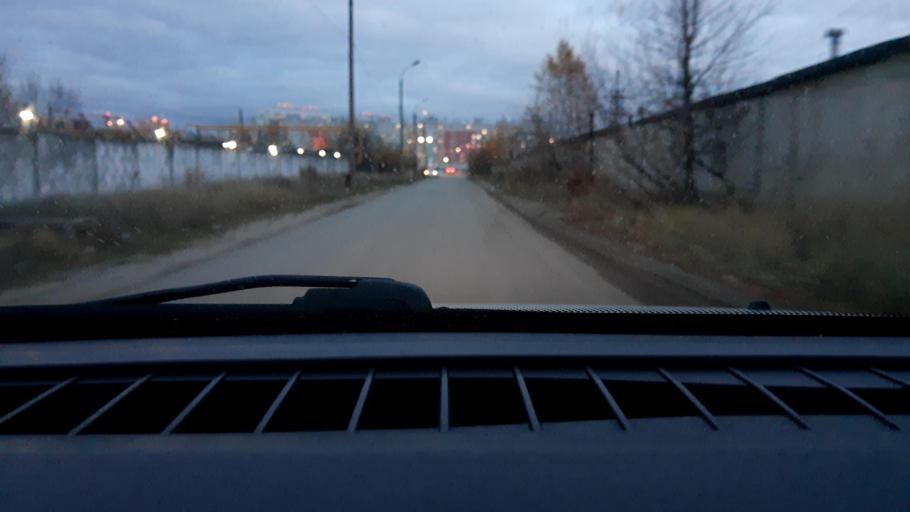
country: RU
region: Nizjnij Novgorod
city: Gorbatovka
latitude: 56.3628
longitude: 43.7904
